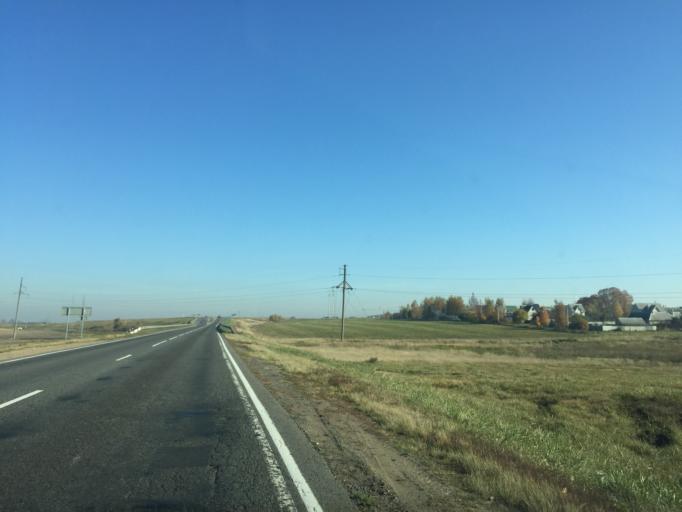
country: BY
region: Mogilev
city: Buynichy
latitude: 53.9436
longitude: 30.2149
